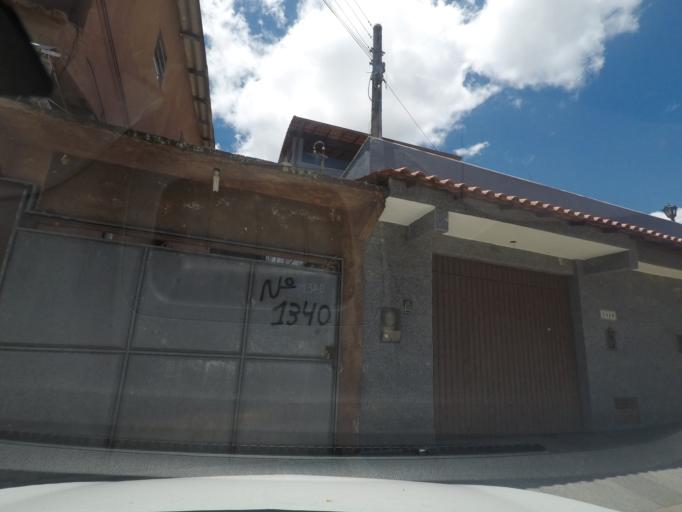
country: BR
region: Rio de Janeiro
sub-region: Teresopolis
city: Teresopolis
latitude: -22.4330
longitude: -42.9725
